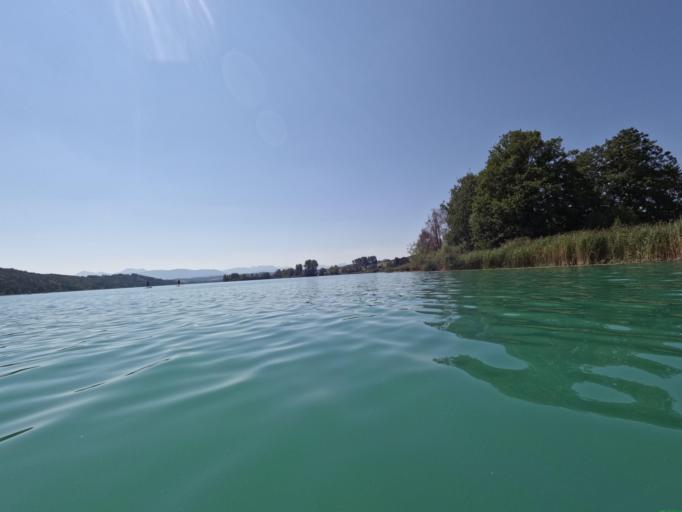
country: DE
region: Bavaria
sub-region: Upper Bavaria
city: Taching am See
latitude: 47.9863
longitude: 12.7420
